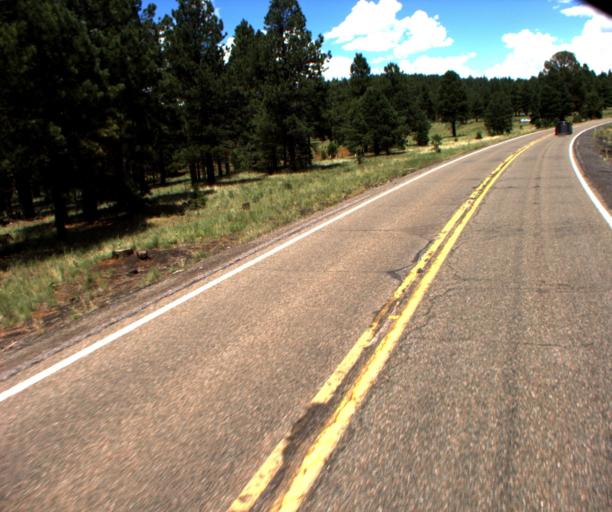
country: US
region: Arizona
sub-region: Coconino County
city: Parks
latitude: 35.3766
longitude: -111.7895
